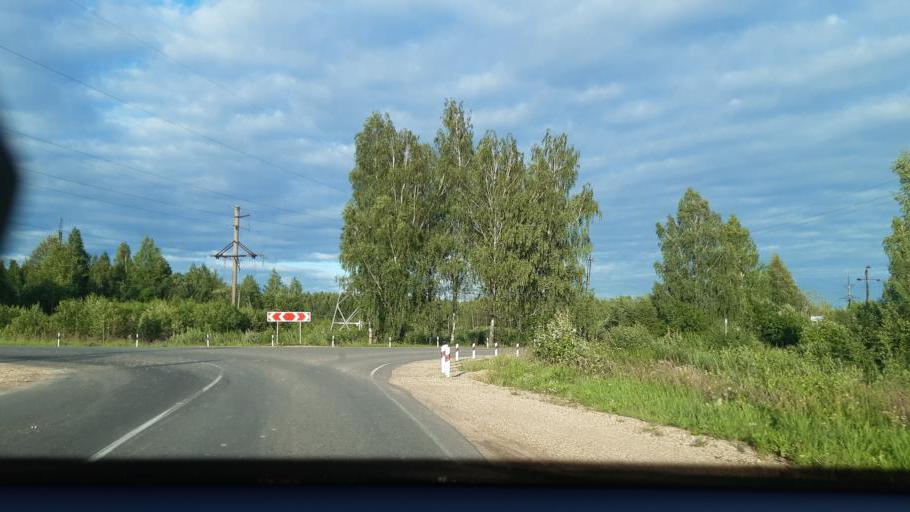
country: RU
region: Smolensk
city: Yel'nya
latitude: 54.5947
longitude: 33.1888
